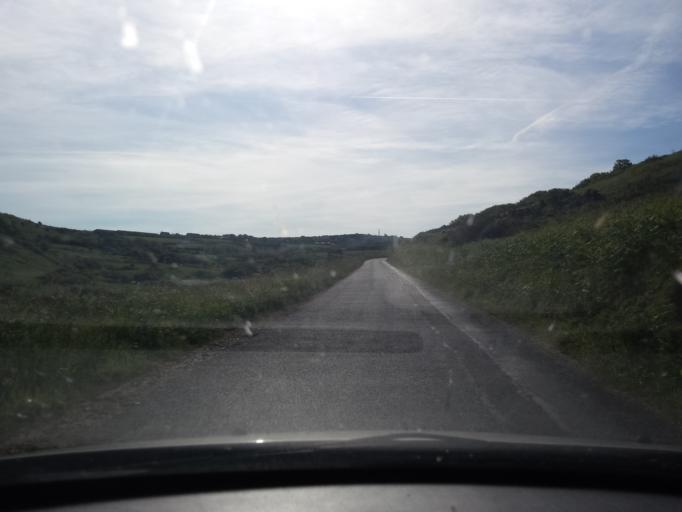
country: FR
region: Lower Normandy
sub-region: Departement de la Manche
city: Beaumont-Hague
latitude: 49.6886
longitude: -1.9315
